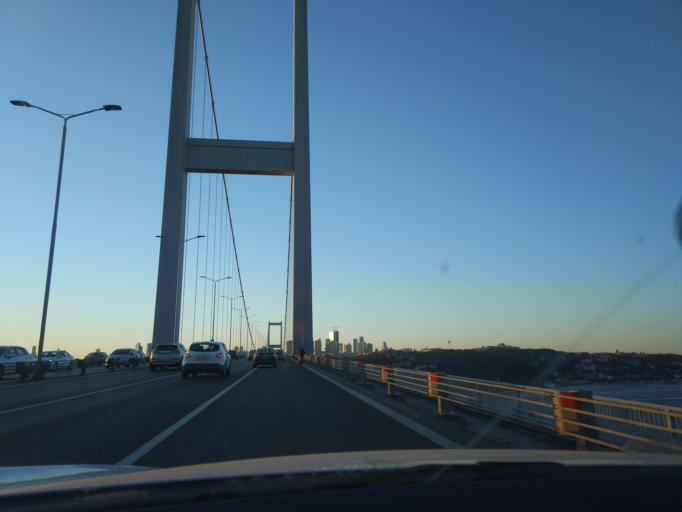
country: TR
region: Istanbul
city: UEskuedar
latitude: 41.0410
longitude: 29.0392
